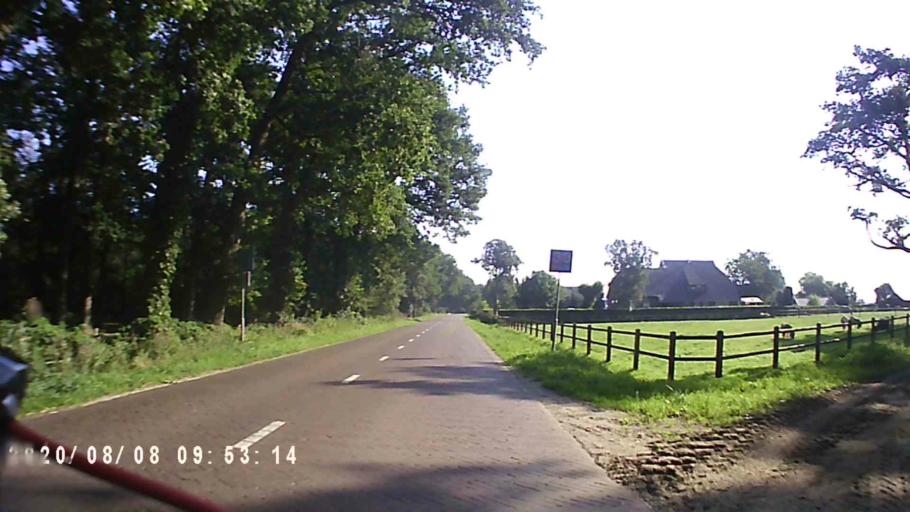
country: NL
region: Groningen
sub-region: Gemeente Leek
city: Leek
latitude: 53.0899
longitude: 6.3888
